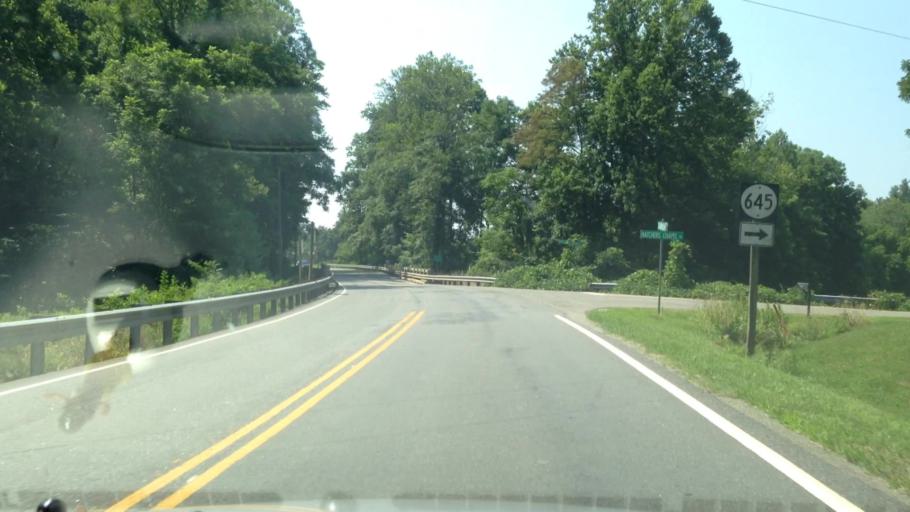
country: US
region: Virginia
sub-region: Patrick County
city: Stuart
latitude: 36.5788
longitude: -80.3809
